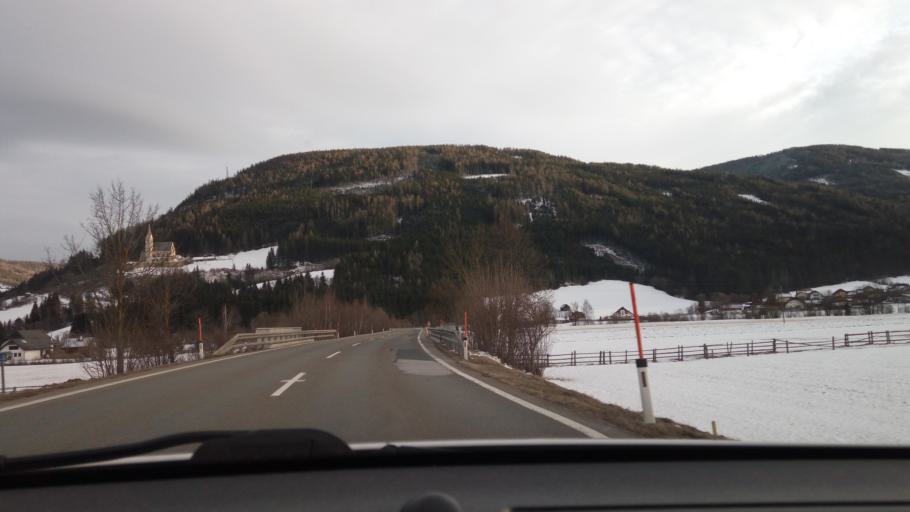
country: AT
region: Salzburg
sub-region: Politischer Bezirk Tamsweg
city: Tamsweg
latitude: 47.1302
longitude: 13.7952
